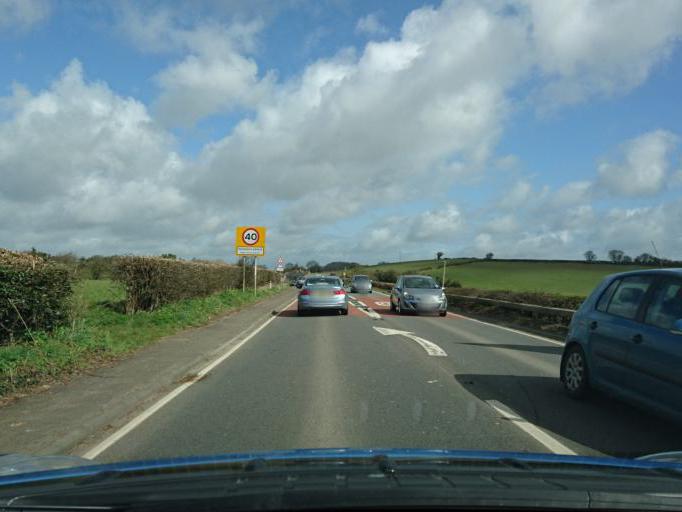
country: GB
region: England
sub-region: South Gloucestershire
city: Cold Ashton
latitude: 51.4555
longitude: -2.3693
